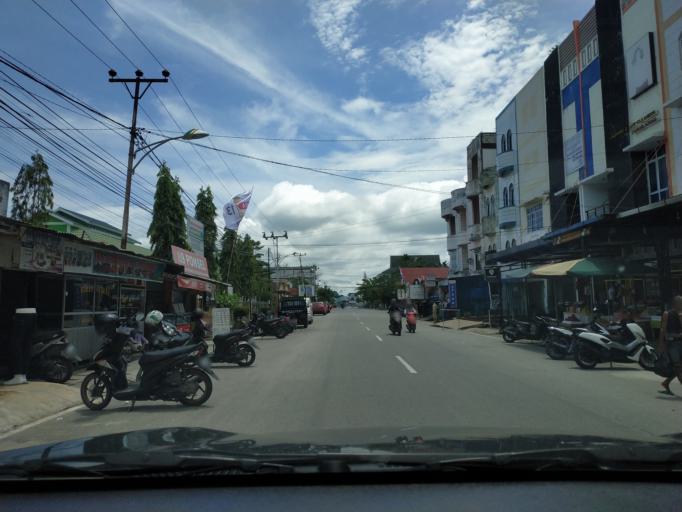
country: ID
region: Riau
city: Tembilahan
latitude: -0.3244
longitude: 103.1590
